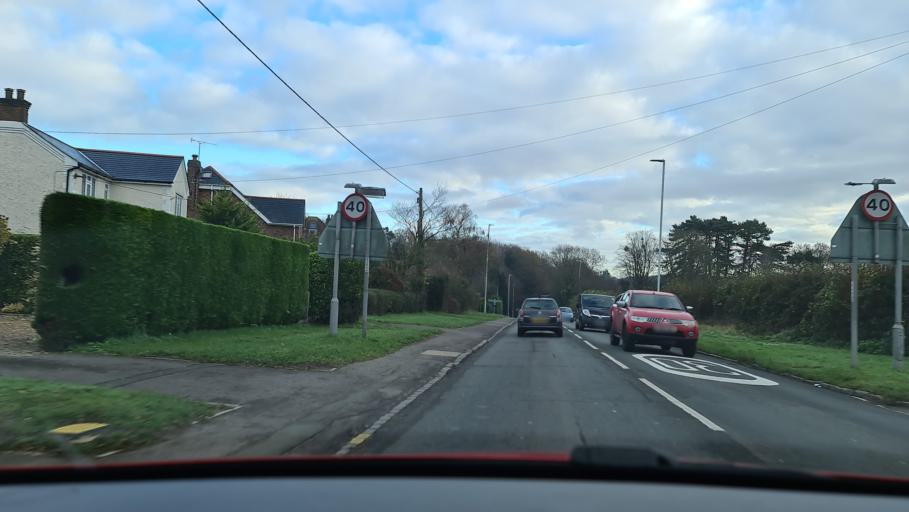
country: GB
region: England
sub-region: Buckinghamshire
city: High Wycombe
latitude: 51.6529
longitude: -0.7095
